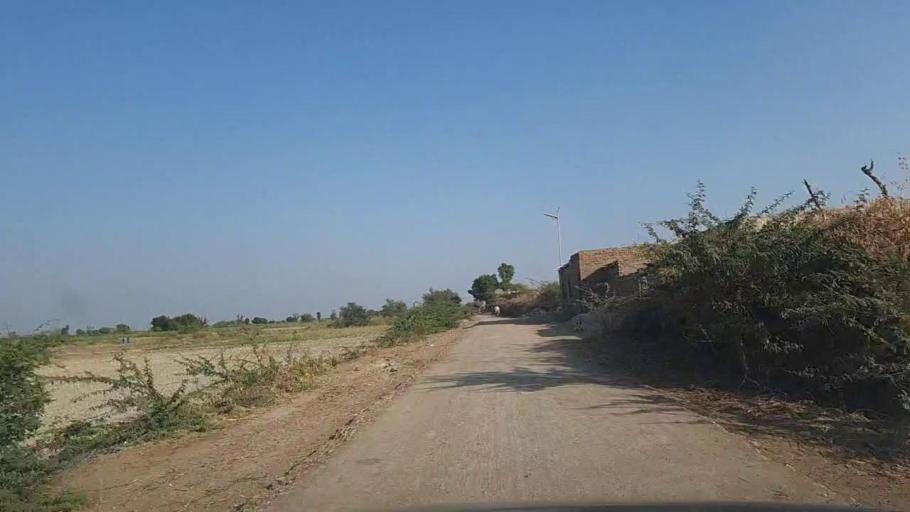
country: PK
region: Sindh
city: Digri
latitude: 25.0405
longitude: 69.2672
